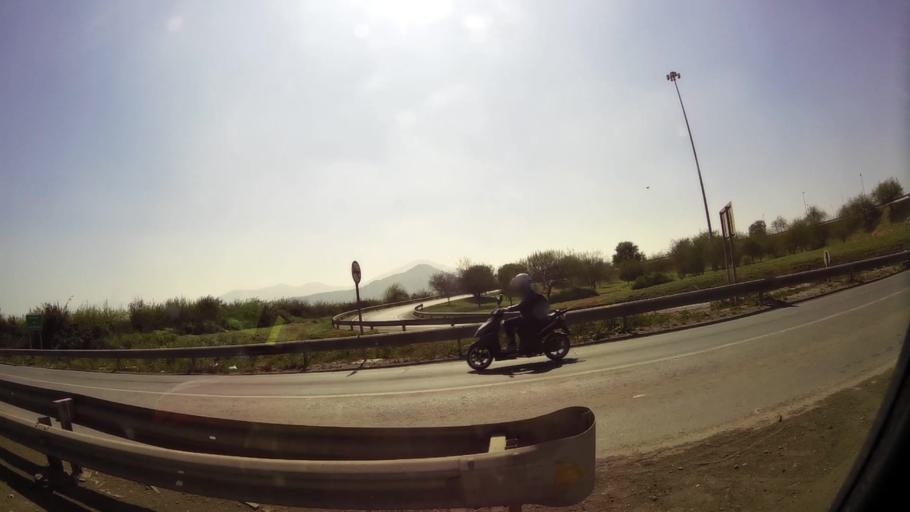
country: CL
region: Santiago Metropolitan
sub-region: Provincia de Santiago
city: Lo Prado
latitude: -33.5079
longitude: -70.8000
